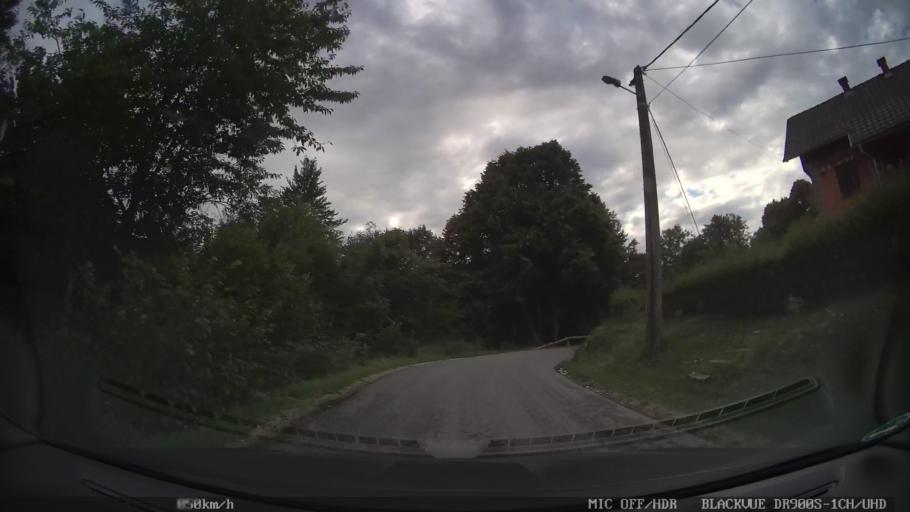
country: HR
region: Licko-Senjska
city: Jezerce
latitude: 44.9244
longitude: 15.5904
